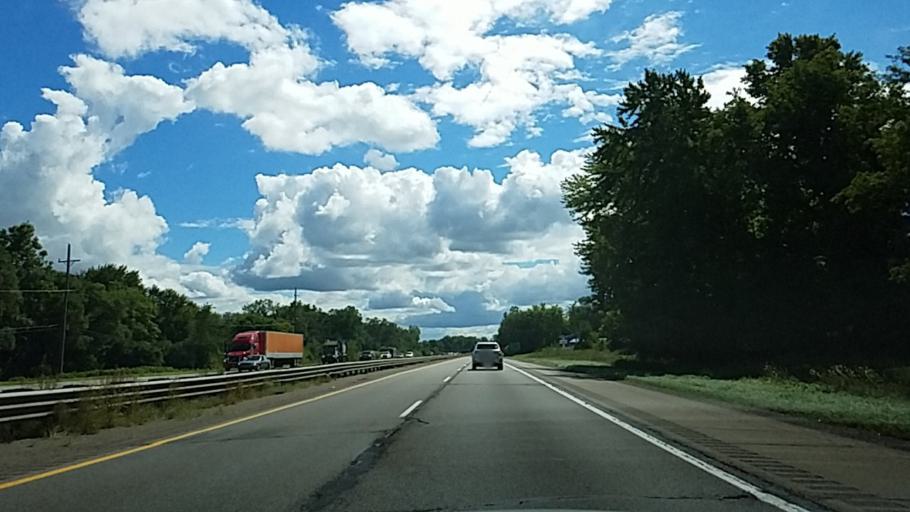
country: US
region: Michigan
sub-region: Livingston County
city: Whitmore Lake
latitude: 42.4026
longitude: -83.7629
